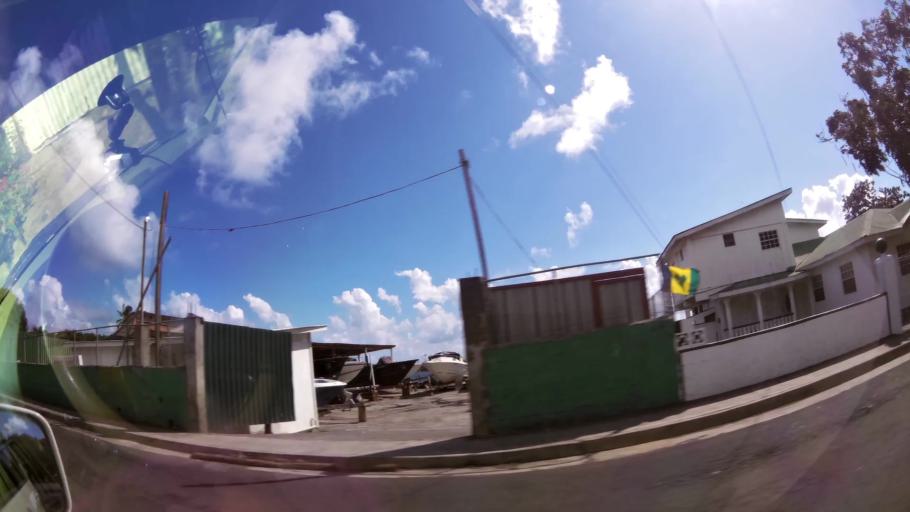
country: VC
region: Saint George
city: Kingstown
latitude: 13.1319
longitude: -61.1975
